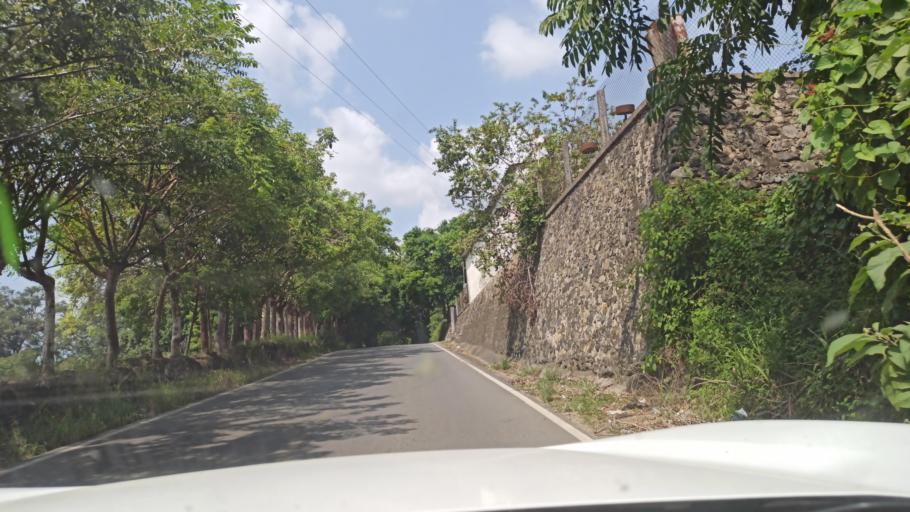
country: MX
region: Veracruz
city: Martinez de la Torre
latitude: 20.0818
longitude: -97.0703
